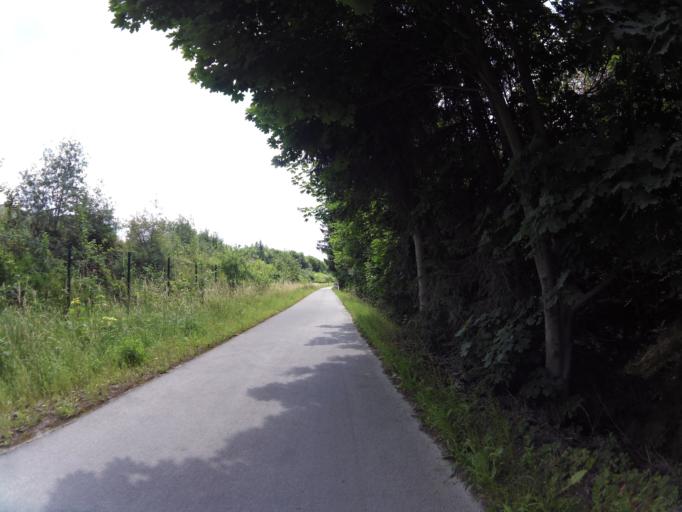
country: DE
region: Thuringia
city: Gorkwitz
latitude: 50.5453
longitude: 11.7605
